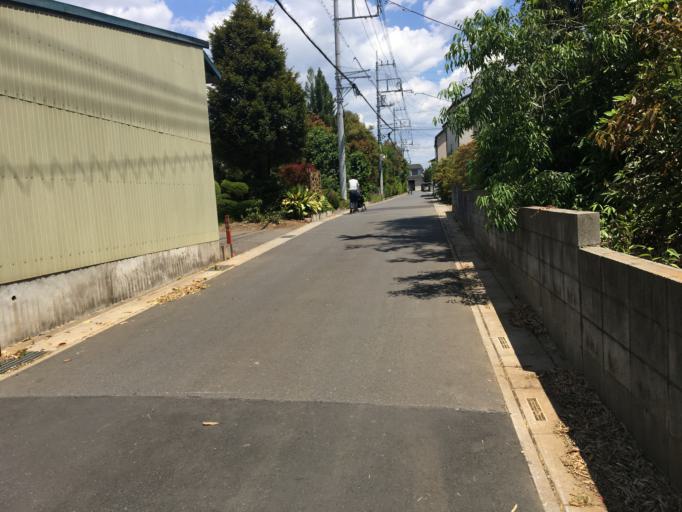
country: JP
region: Saitama
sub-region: Kawaguchi-shi
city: Hatogaya-honcho
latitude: 35.8466
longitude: 139.7505
